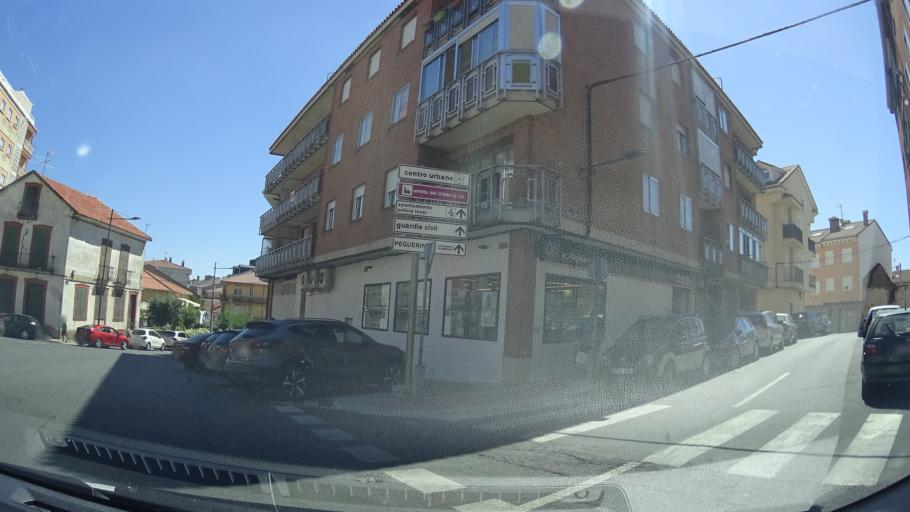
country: ES
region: Castille and Leon
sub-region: Provincia de Avila
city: Las Navas del Marques
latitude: 40.6022
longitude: -4.3342
